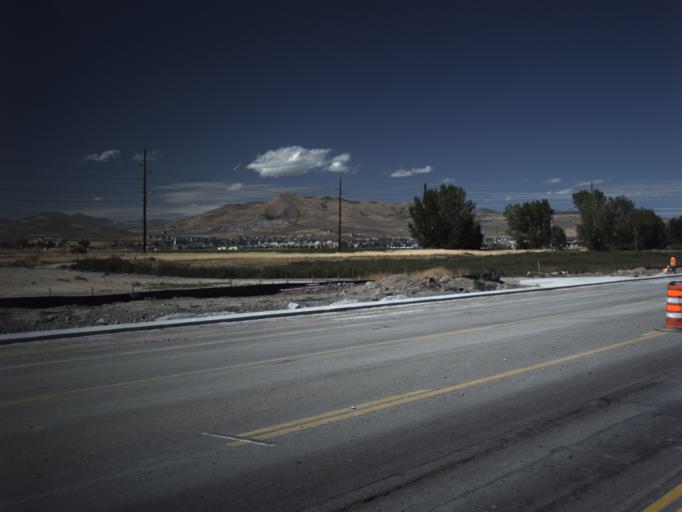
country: US
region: Utah
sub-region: Utah County
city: Saratoga Springs
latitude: 40.3519
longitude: -111.9163
